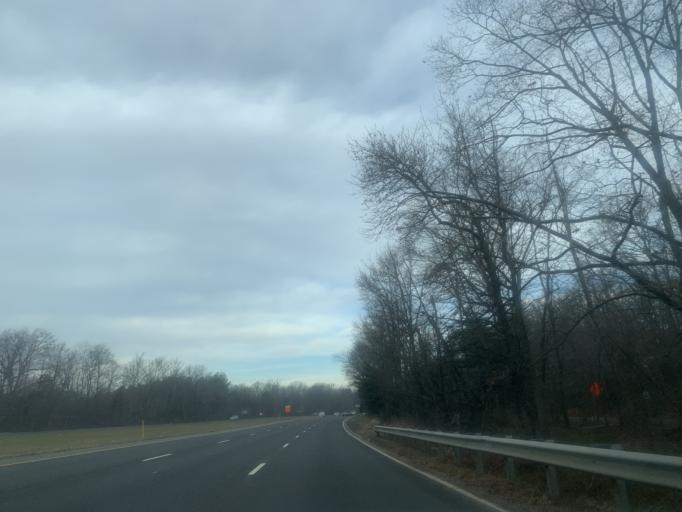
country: US
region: Maryland
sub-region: Prince George's County
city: Mellwood
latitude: 38.8215
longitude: -76.8490
